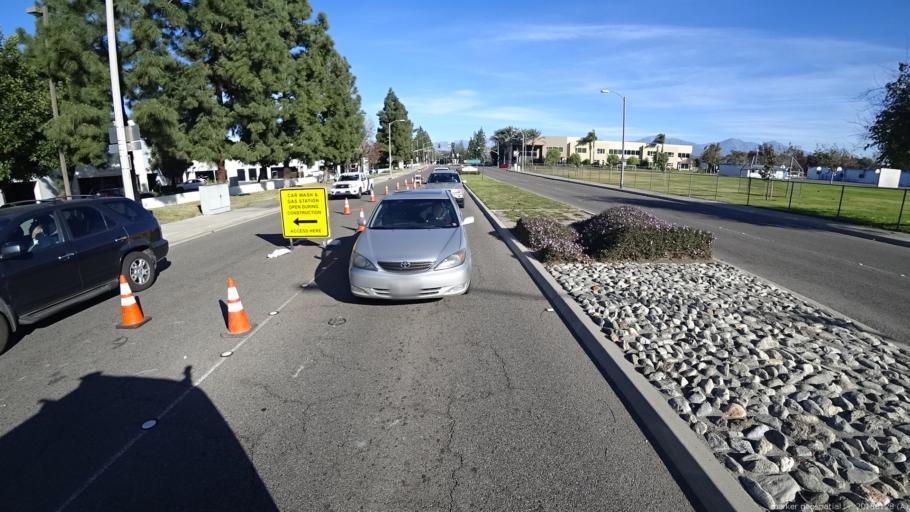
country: US
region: California
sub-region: Los Angeles County
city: Walnut
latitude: 34.0019
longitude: -117.8553
